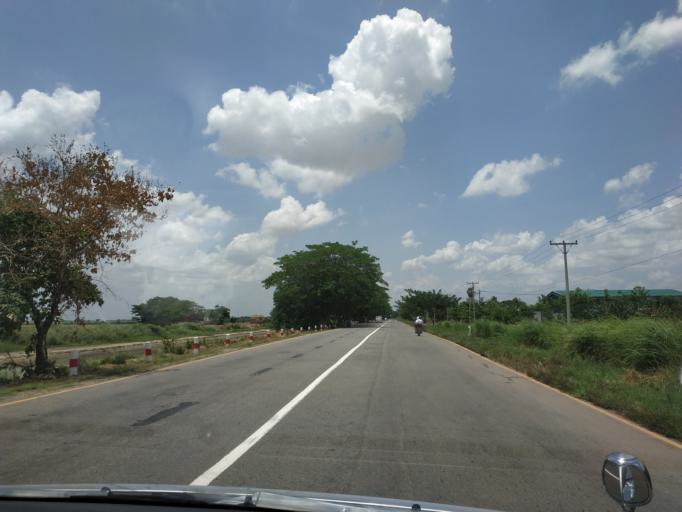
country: MM
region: Bago
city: Thanatpin
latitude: 17.4961
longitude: 96.6903
